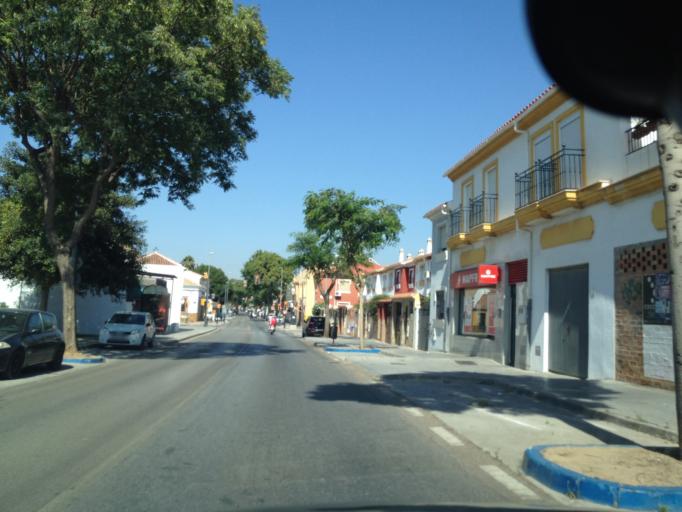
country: ES
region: Andalusia
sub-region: Provincia de Malaga
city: Alhaurin de la Torre
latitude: 36.7220
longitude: -4.5363
